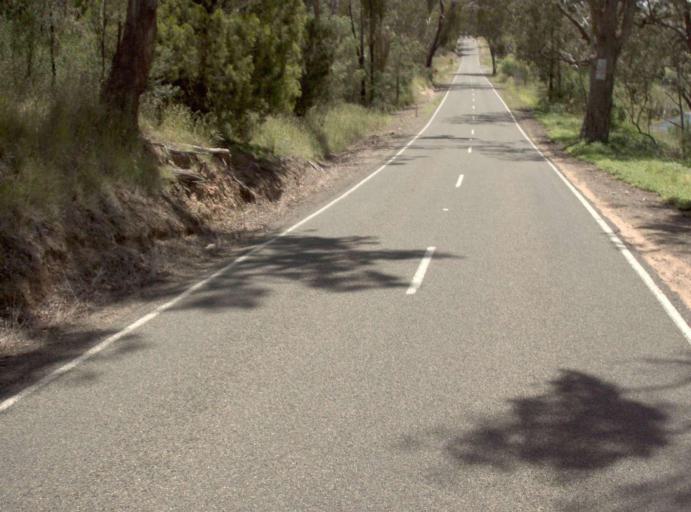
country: AU
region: Victoria
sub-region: East Gippsland
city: Bairnsdale
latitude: -37.4121
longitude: 147.8347
